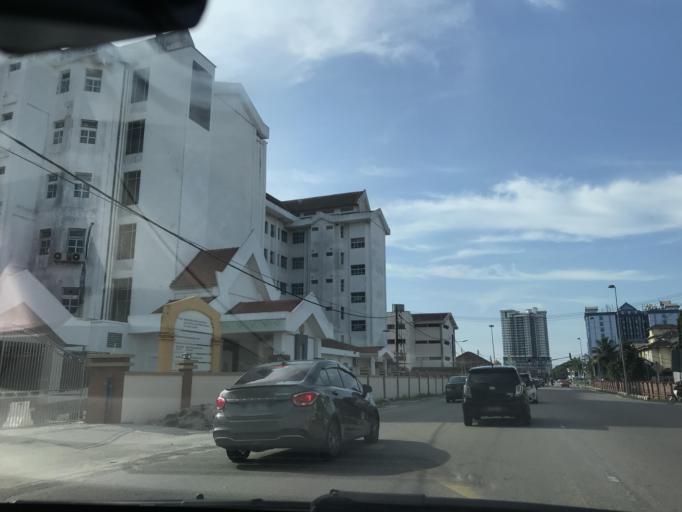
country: MY
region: Kelantan
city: Kota Bharu
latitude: 6.1232
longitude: 102.2471
